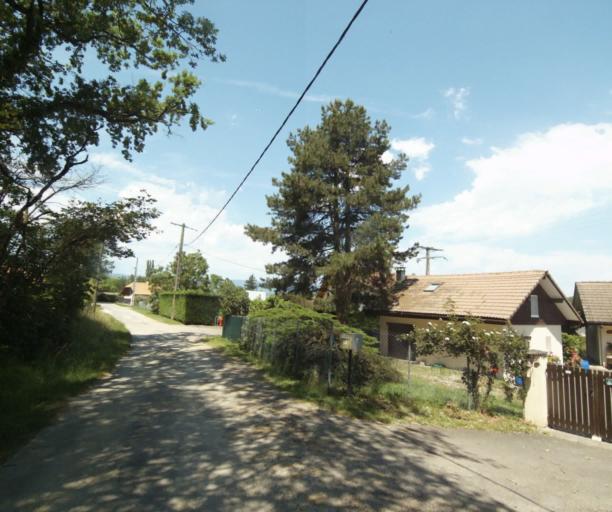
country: FR
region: Rhone-Alpes
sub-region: Departement de la Haute-Savoie
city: Messery
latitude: 46.3660
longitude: 6.3408
